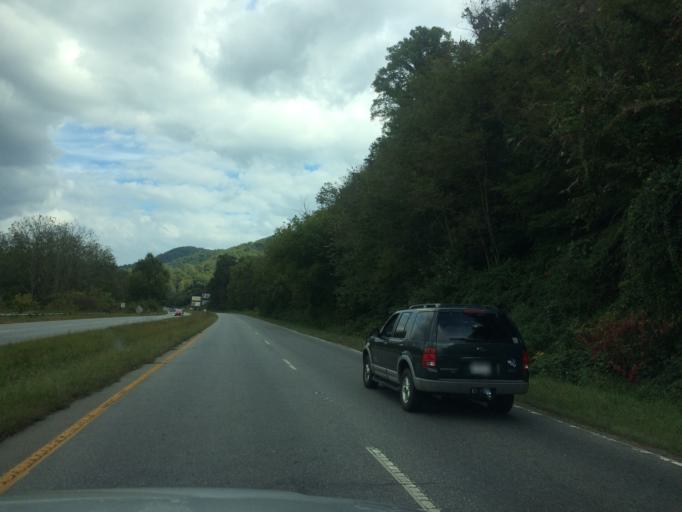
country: US
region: North Carolina
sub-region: Haywood County
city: Clyde
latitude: 35.5313
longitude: -82.9026
